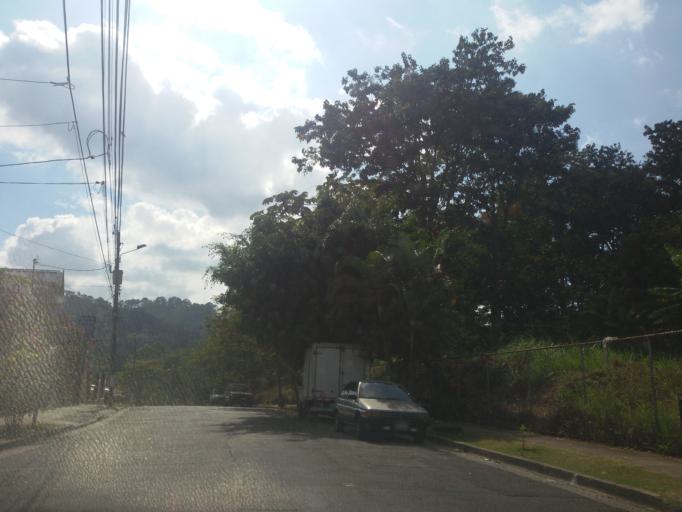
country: CR
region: San Jose
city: Curridabat
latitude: 9.9089
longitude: -84.0307
